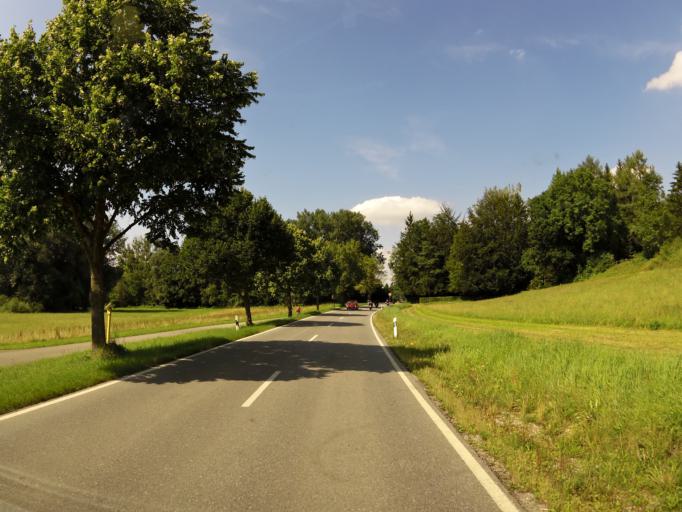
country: DE
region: Bavaria
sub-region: Upper Bavaria
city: Andechs
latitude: 47.9392
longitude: 11.1522
